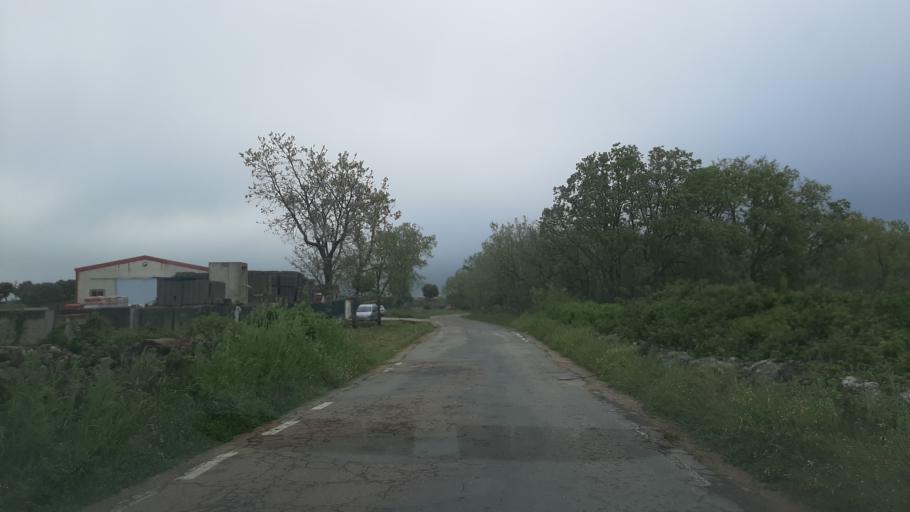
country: ES
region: Castille and Leon
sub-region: Provincia de Salamanca
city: Endrinal
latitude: 40.5545
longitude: -5.8069
